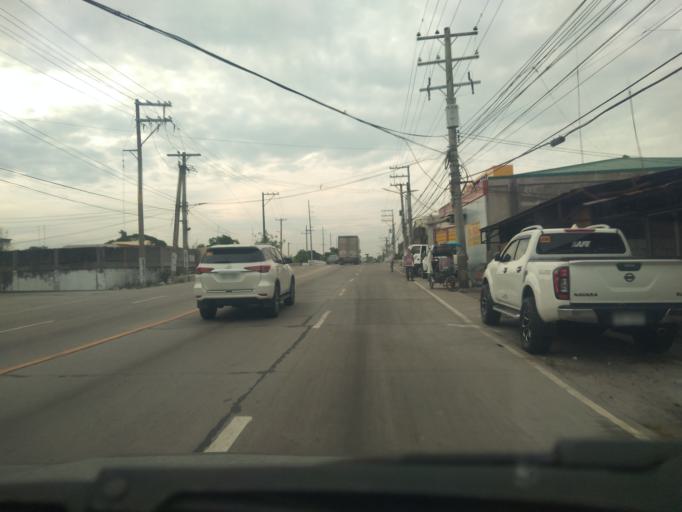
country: PH
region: Central Luzon
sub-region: Province of Pampanga
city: San Fernando
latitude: 15.0287
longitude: 120.6970
